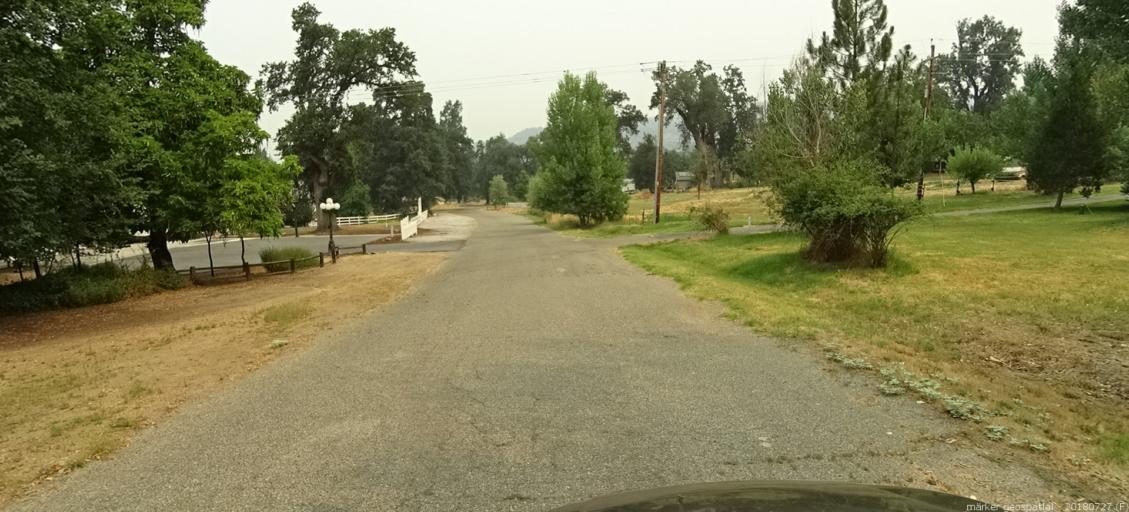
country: US
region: California
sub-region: Madera County
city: Oakhurst
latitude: 37.3222
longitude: -119.6264
